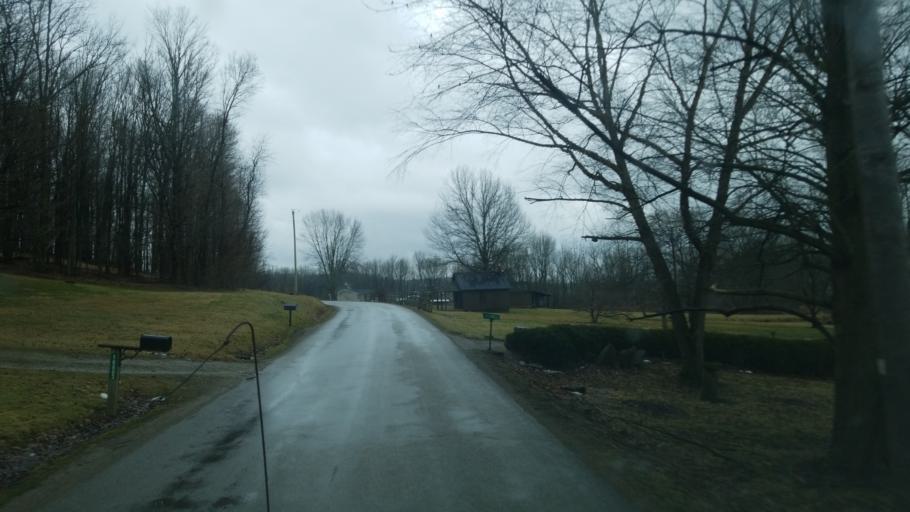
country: US
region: Ohio
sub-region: Knox County
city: Mount Vernon
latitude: 40.4515
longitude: -82.4484
